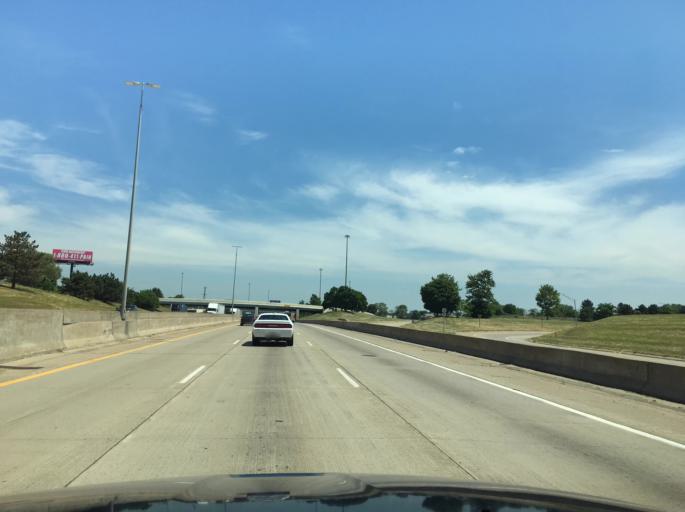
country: US
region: Michigan
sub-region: Wayne County
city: Dearborn
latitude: 42.3224
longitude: -83.1639
